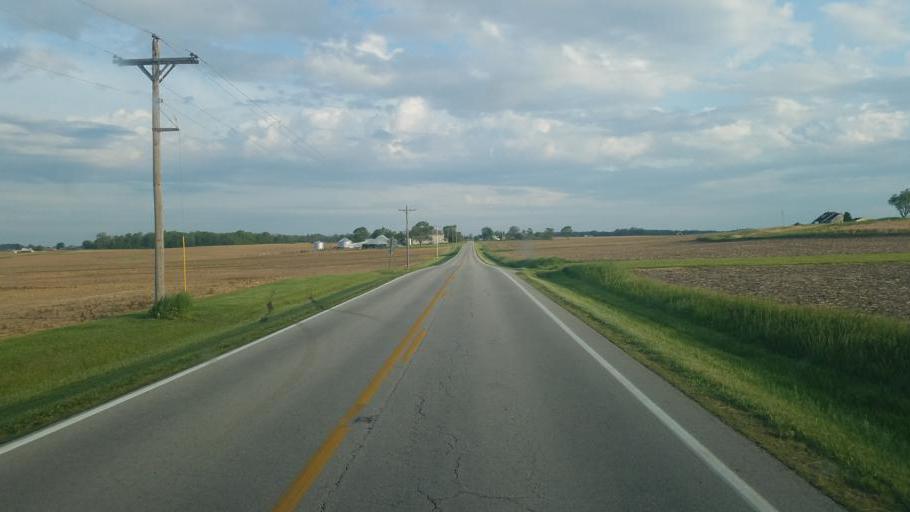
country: US
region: Ohio
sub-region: Highland County
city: Leesburg
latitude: 39.4020
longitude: -83.6012
